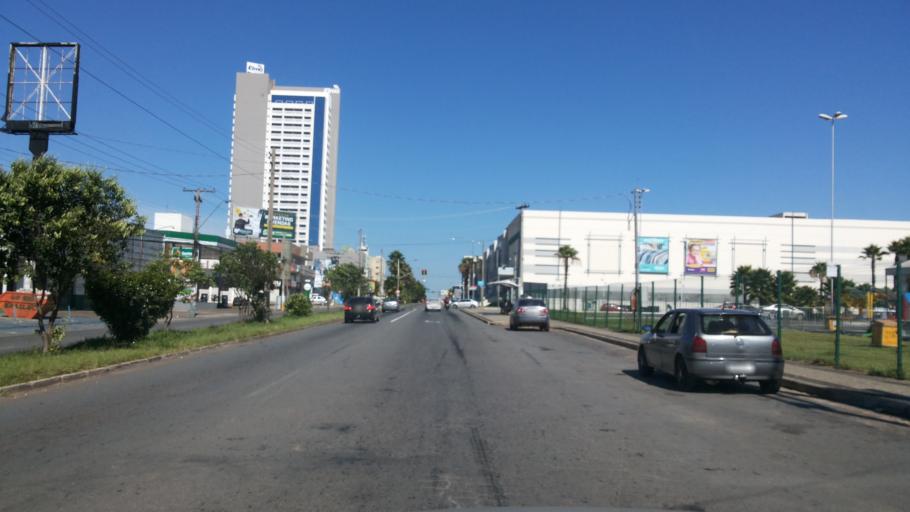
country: BR
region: Goias
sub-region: Goiania
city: Goiania
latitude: -16.7409
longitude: -49.2746
